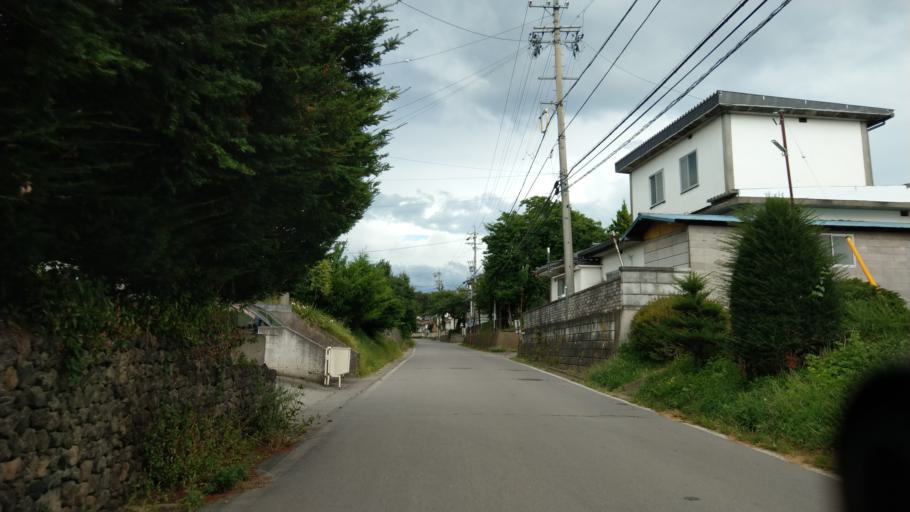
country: JP
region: Nagano
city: Komoro
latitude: 36.3125
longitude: 138.4617
